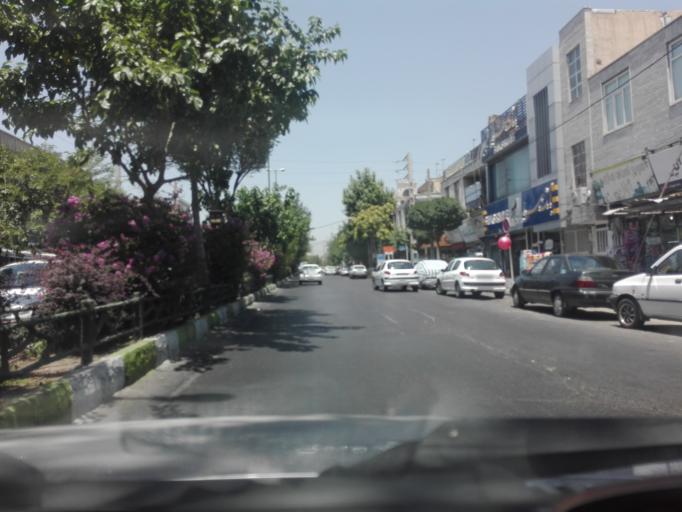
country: IR
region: Tehran
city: Shahre Jadide Andisheh
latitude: 35.7309
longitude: 50.9902
